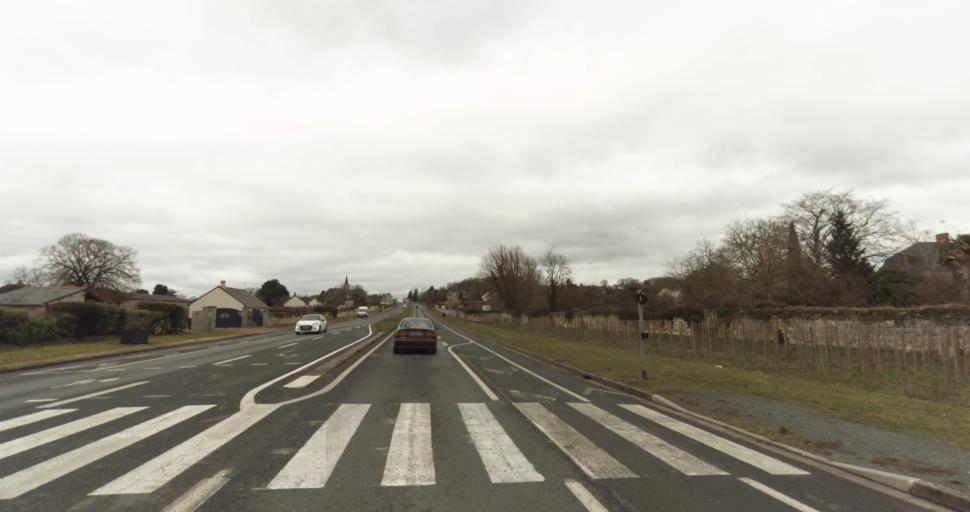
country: FR
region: Pays de la Loire
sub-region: Departement de Maine-et-Loire
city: Varrains
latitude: 47.2230
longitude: -0.0619
